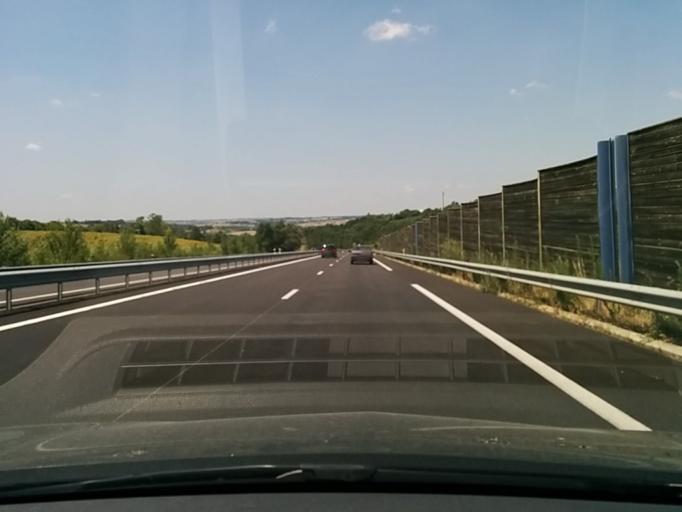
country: FR
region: Midi-Pyrenees
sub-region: Departement du Gers
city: Pujaudran
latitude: 43.5972
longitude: 1.1100
